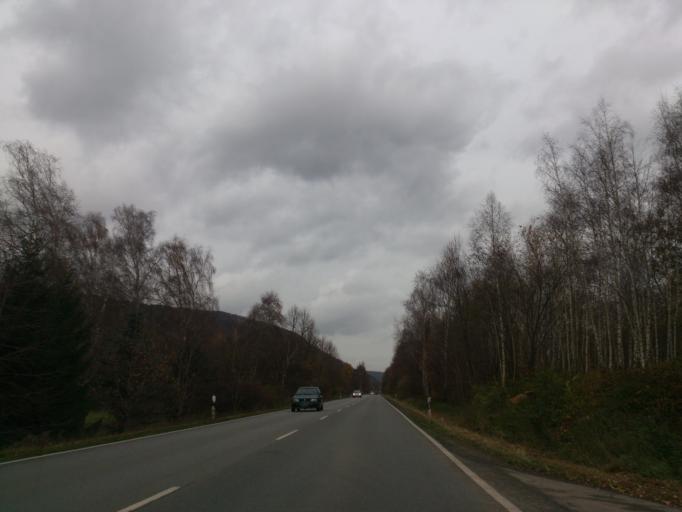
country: DE
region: Lower Saxony
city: Boffzen
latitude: 51.7419
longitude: 9.3666
